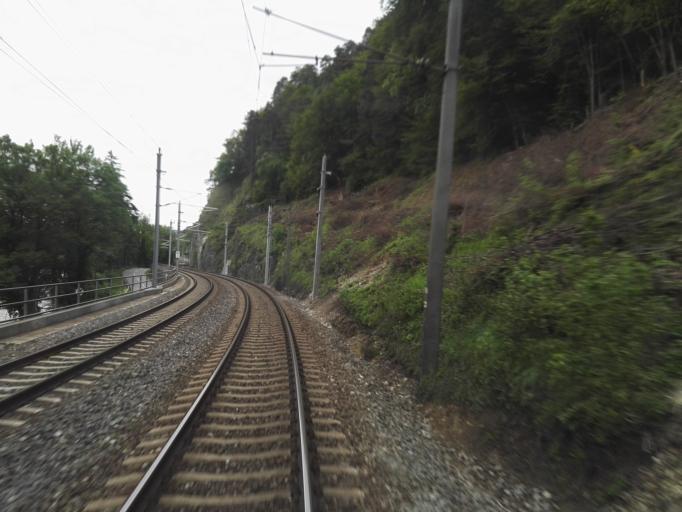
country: AT
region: Styria
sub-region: Politischer Bezirk Graz-Umgebung
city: Deutschfeistritz
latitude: 47.1565
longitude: 15.3164
